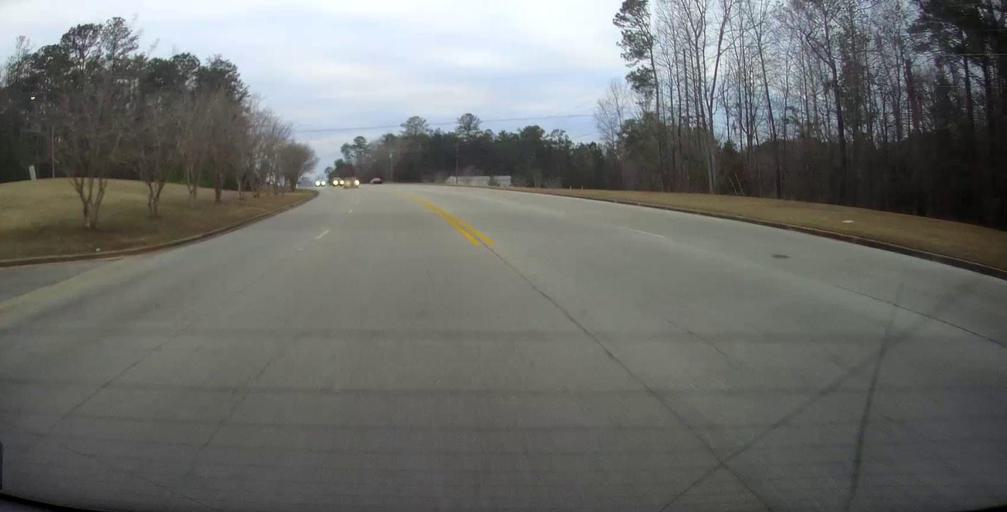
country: US
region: Alabama
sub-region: Chambers County
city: Valley
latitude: 32.8175
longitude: -85.1916
